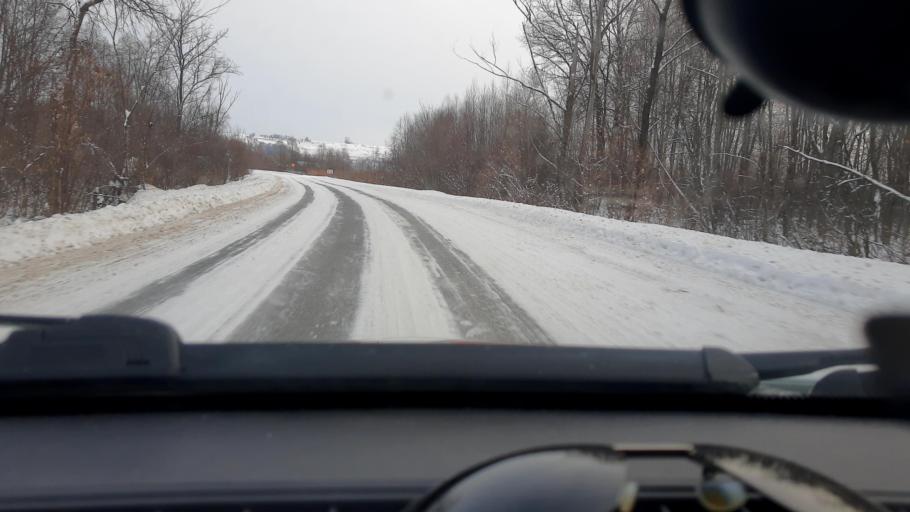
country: RU
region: Bashkortostan
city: Yazykovo
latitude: 55.0263
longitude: 56.2096
